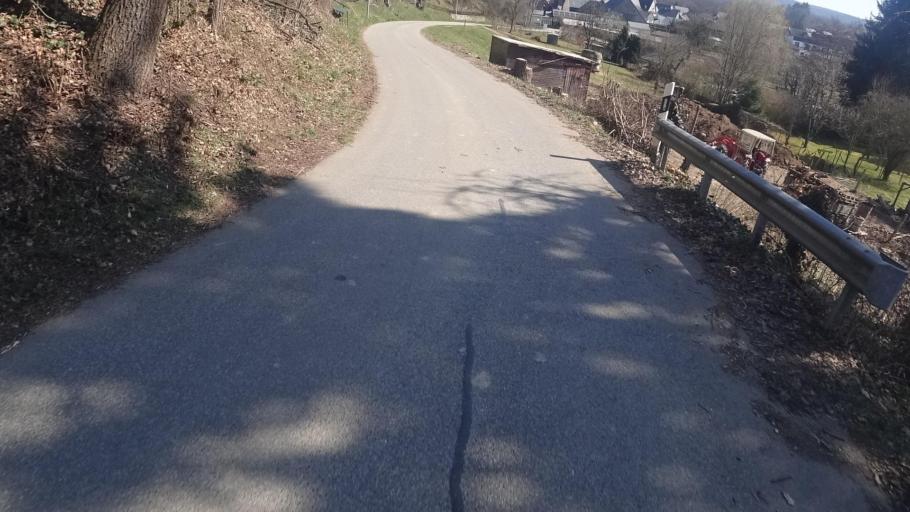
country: DE
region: Rheinland-Pfalz
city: Mengerschied
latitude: 49.9126
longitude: 7.5019
